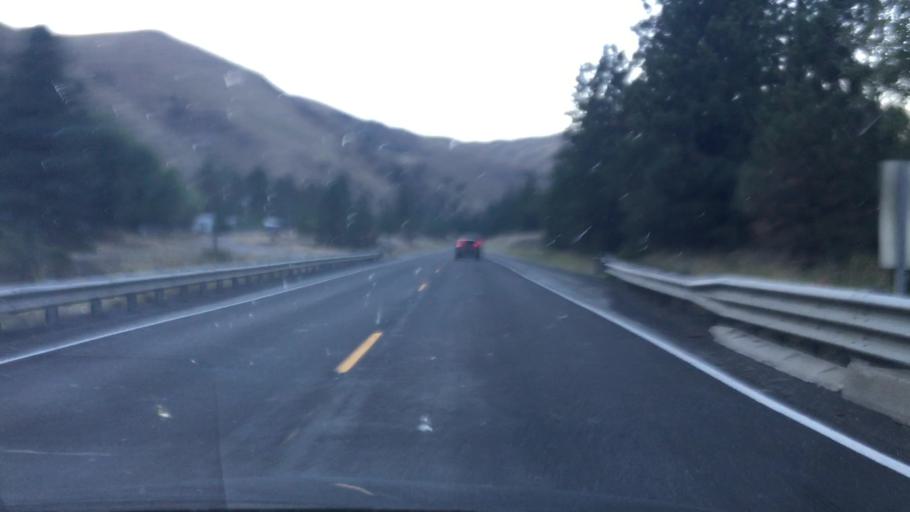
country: US
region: Idaho
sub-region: Valley County
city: McCall
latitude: 45.2970
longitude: -116.3593
